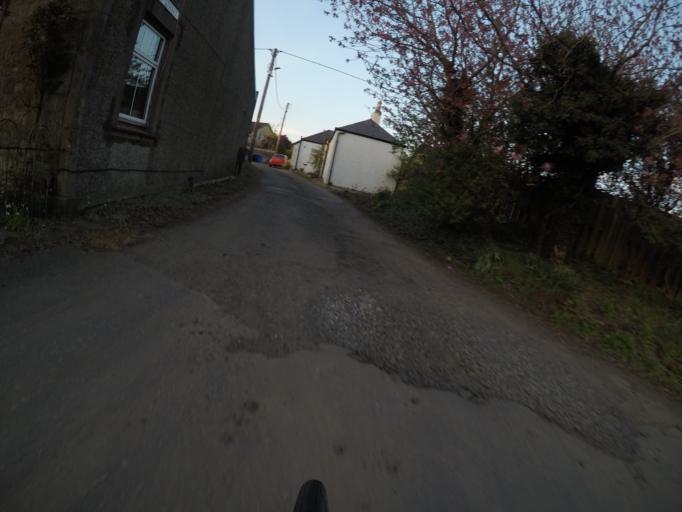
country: GB
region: Scotland
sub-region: South Ayrshire
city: Troon
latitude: 55.5503
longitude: -4.6237
